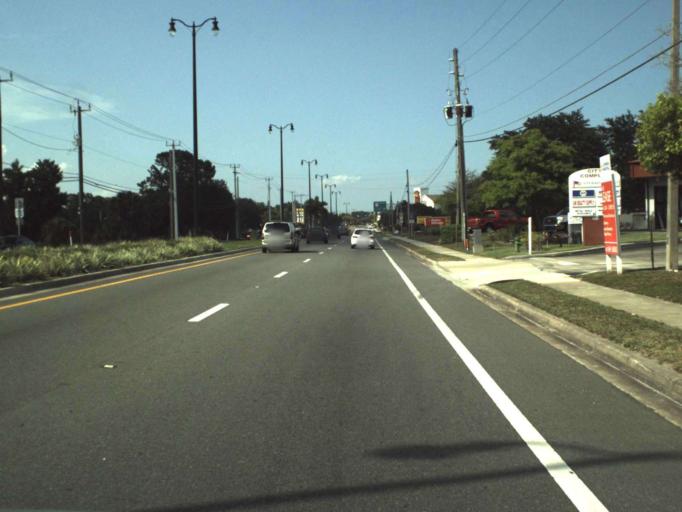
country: US
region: Florida
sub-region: Seminole County
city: Sanford
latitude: 28.7736
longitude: -81.2783
